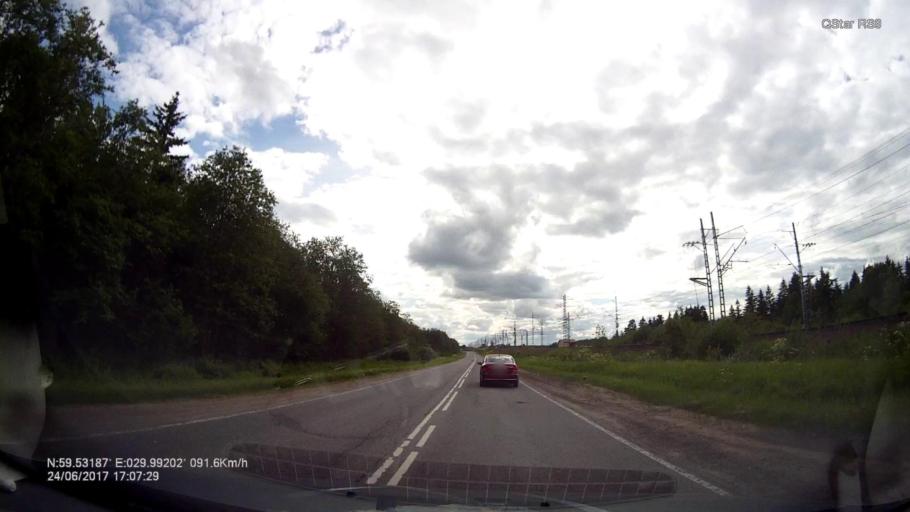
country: RU
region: Leningrad
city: Voyskovitsy
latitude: 59.5317
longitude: 29.9913
